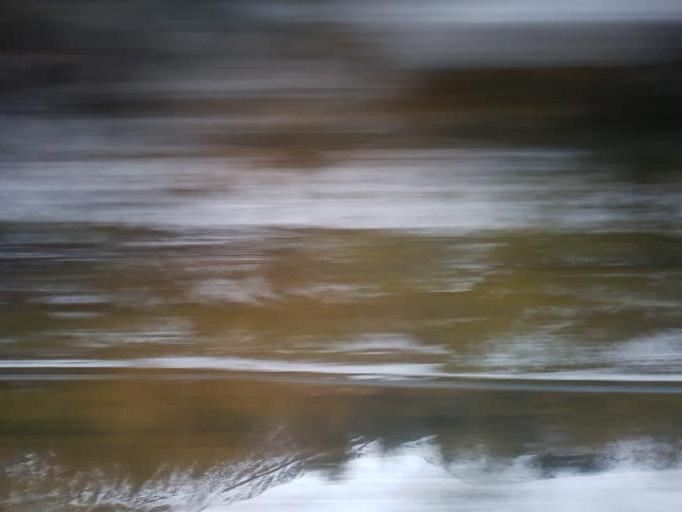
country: NO
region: Sor-Trondelag
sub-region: Oppdal
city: Oppdal
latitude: 62.5310
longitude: 9.6167
